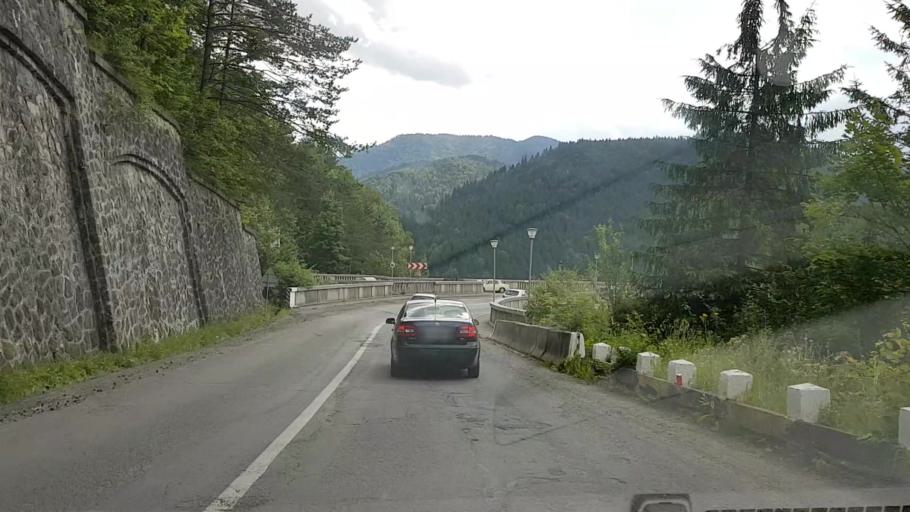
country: RO
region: Neamt
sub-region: Comuna Bicaz
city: Dodeni
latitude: 46.9378
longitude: 26.1058
